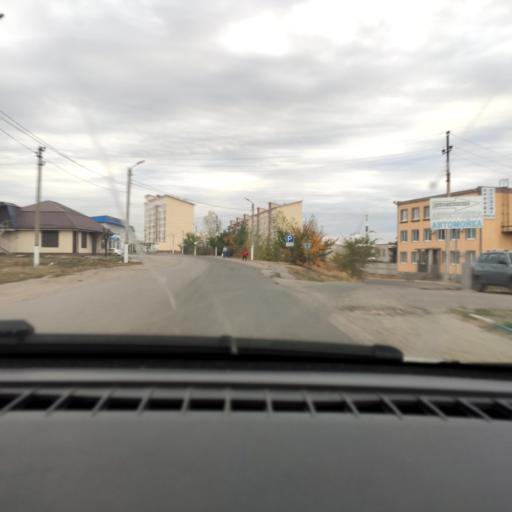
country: RU
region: Voronezj
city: Novaya Usman'
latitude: 51.6101
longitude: 39.3879
